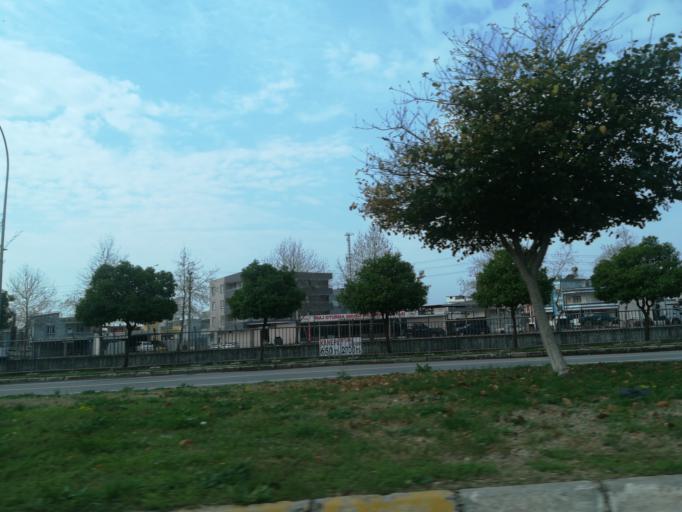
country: TR
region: Adana
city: Yuregir
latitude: 36.9888
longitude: 35.3654
